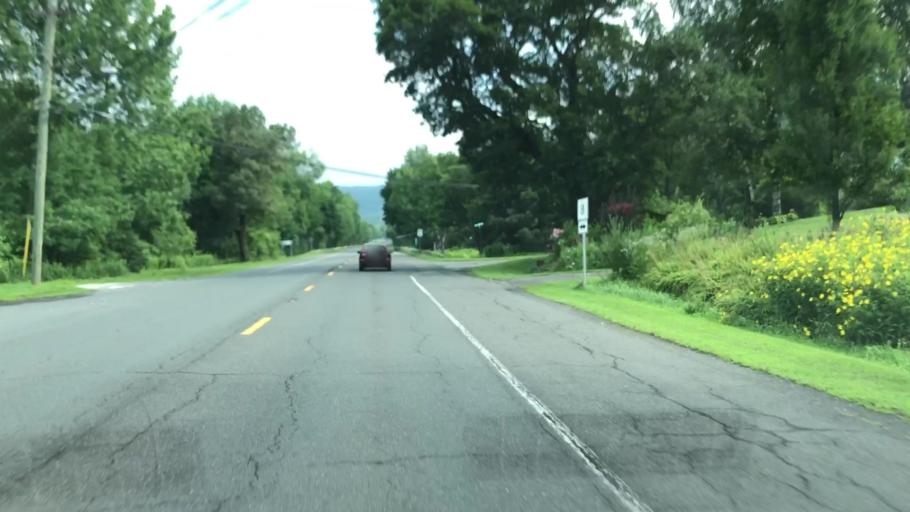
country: US
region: Massachusetts
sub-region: Berkshire County
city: Lanesborough
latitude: 42.5125
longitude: -73.1926
